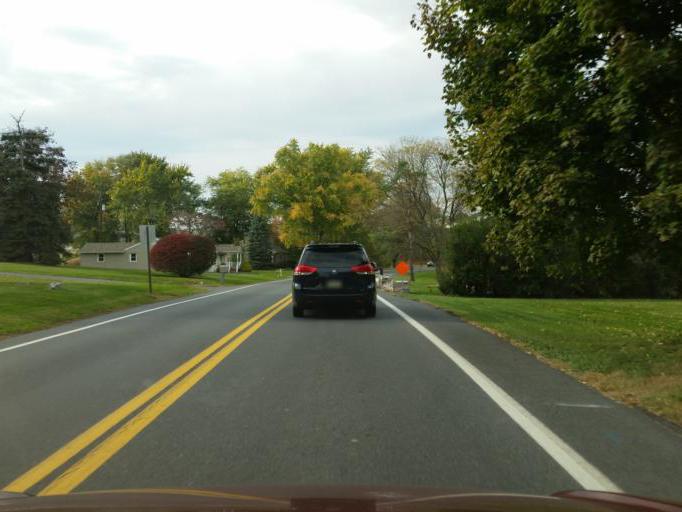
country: US
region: Pennsylvania
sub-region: Dauphin County
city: Hershey
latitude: 40.2561
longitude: -76.6329
